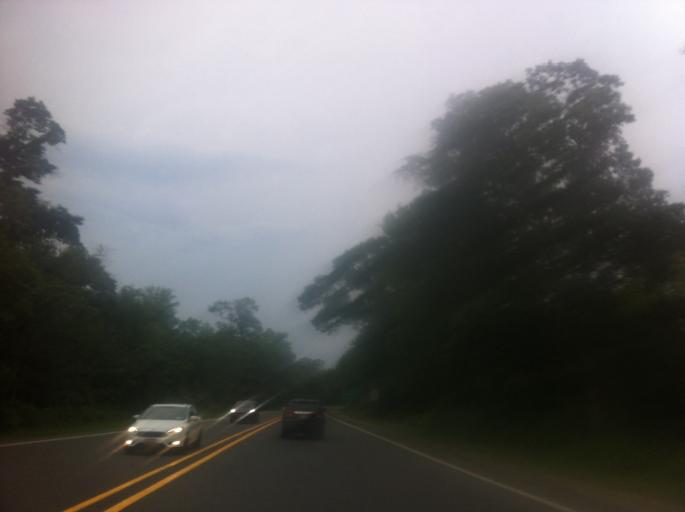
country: US
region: New York
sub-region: Nassau County
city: North Massapequa
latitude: 40.7068
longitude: -73.4513
